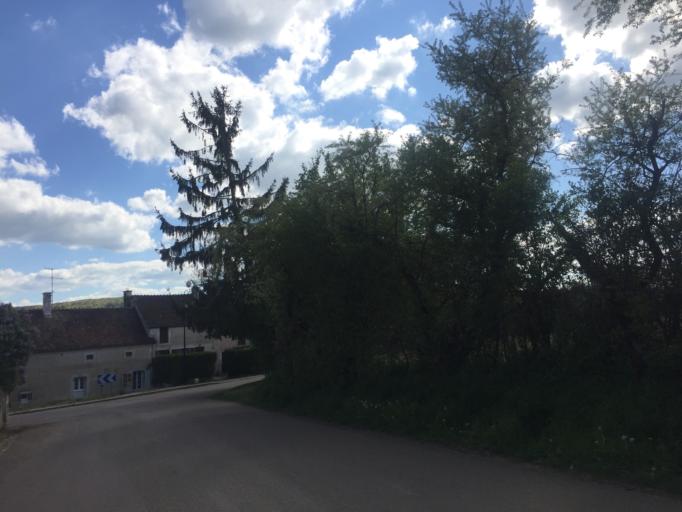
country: FR
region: Bourgogne
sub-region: Departement de l'Yonne
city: Fontenailles
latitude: 47.5604
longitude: 3.3247
